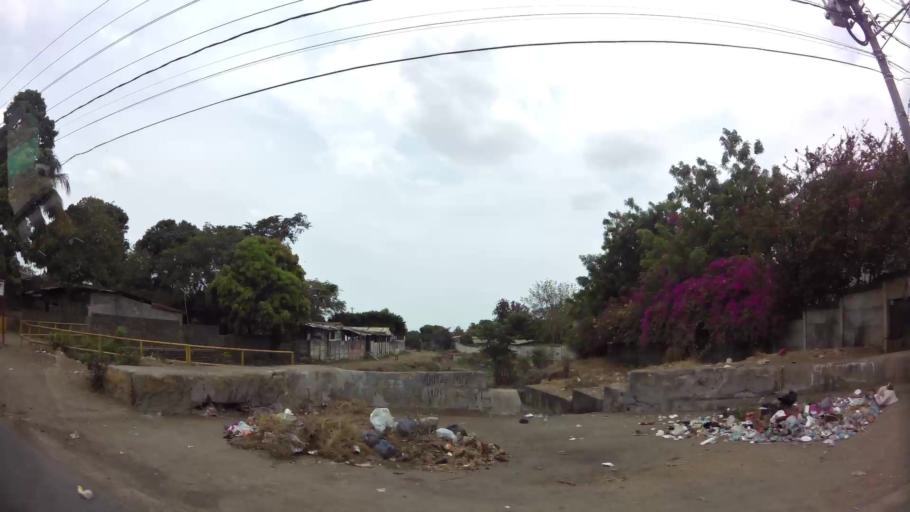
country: NI
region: Managua
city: Managua
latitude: 12.1094
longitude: -86.2251
